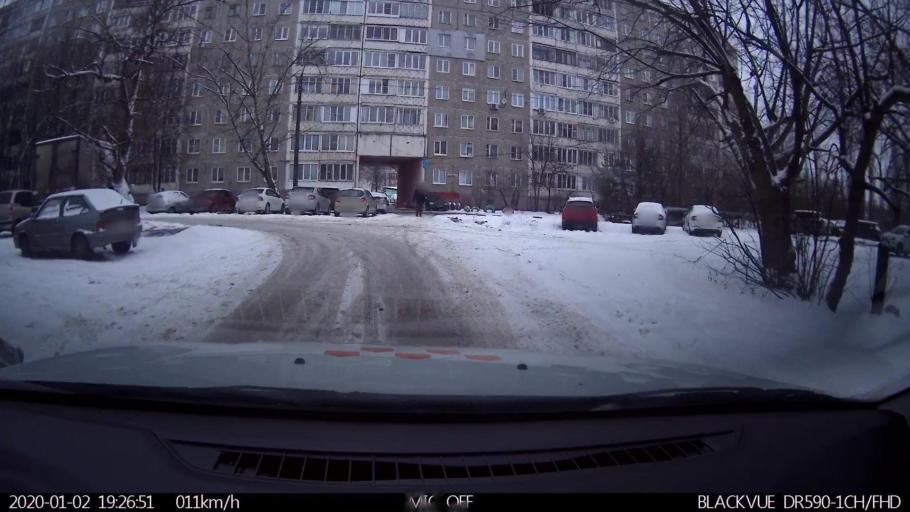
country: RU
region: Nizjnij Novgorod
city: Nizhniy Novgorod
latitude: 56.3194
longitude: 43.8750
